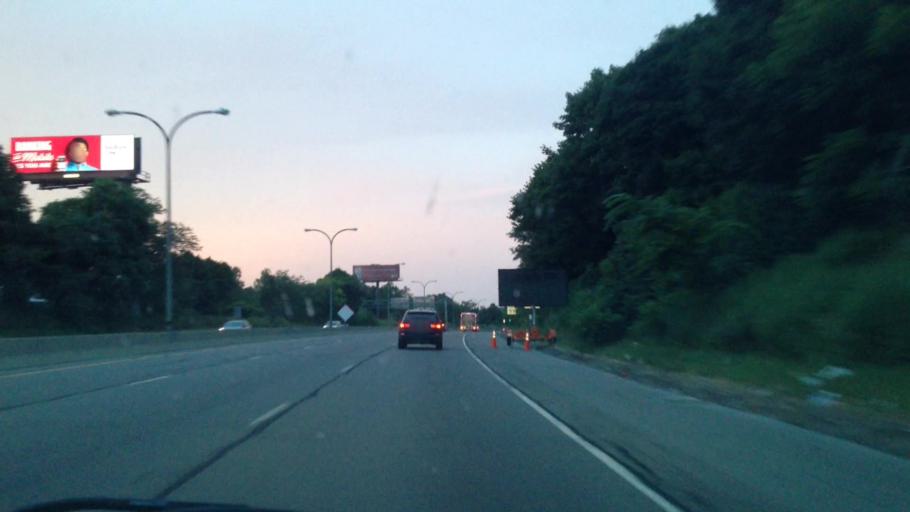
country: US
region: New York
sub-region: Erie County
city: Eggertsville
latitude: 42.9273
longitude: -78.8375
